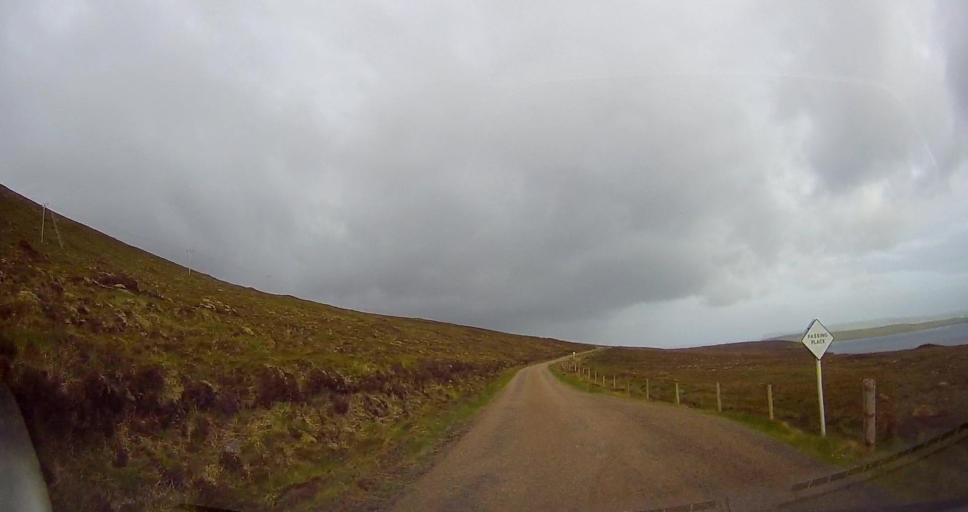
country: GB
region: Scotland
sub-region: Orkney Islands
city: Stromness
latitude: 58.8910
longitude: -3.2593
